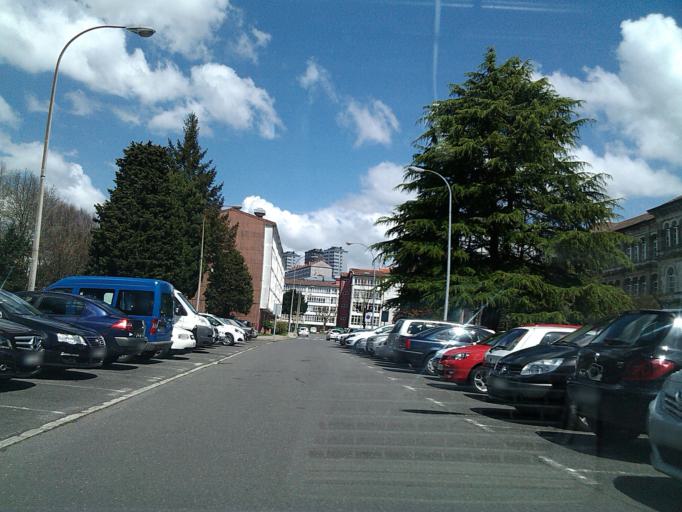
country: ES
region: Galicia
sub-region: Provincia da Coruna
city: Santiago de Compostela
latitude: 42.8897
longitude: -8.5345
